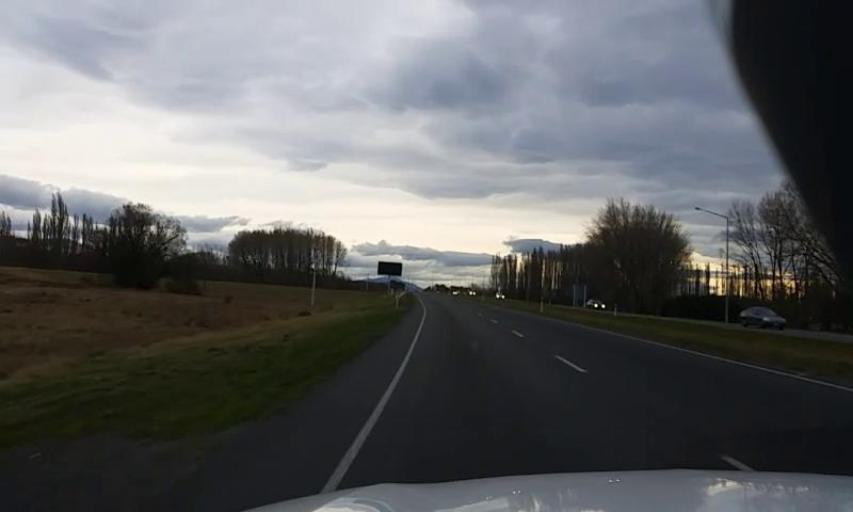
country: NZ
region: Canterbury
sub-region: Waimakariri District
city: Kaiapoi
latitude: -43.4213
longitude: 172.6483
